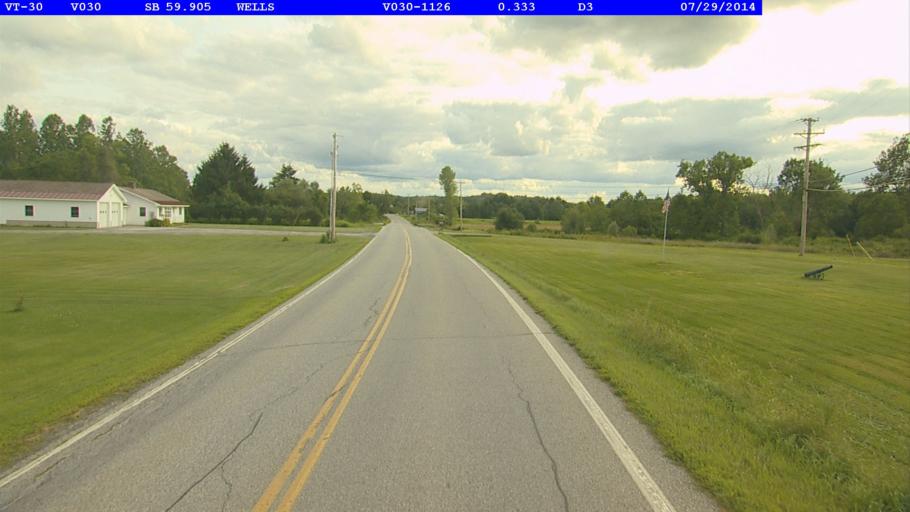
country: US
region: New York
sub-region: Washington County
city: Granville
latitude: 43.4124
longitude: -73.2247
